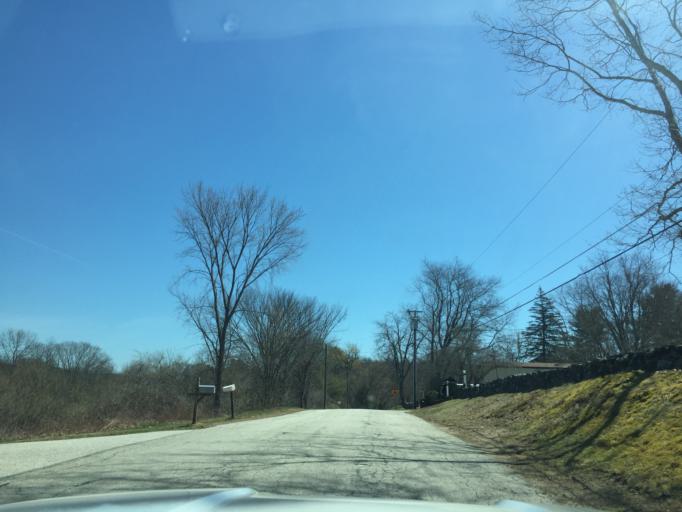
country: US
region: Connecticut
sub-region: Windham County
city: Quinebaug
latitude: 42.0085
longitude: -71.9485
